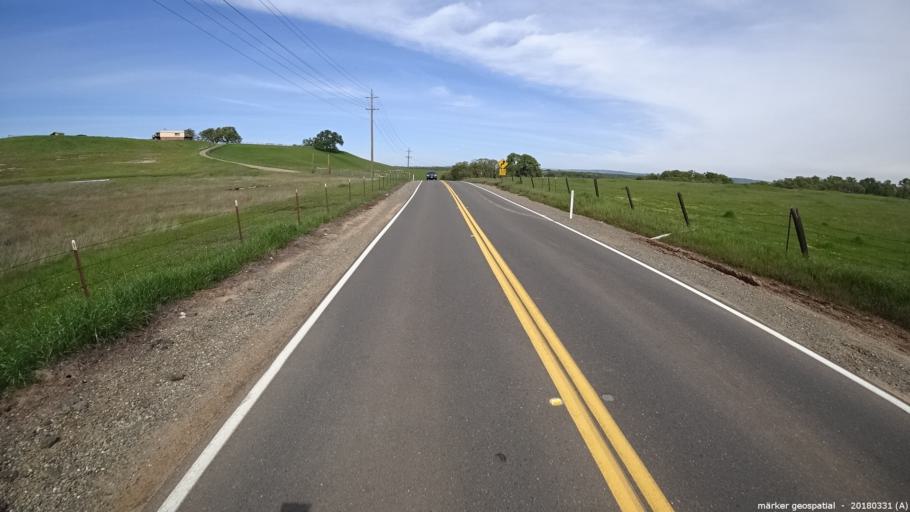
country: US
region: California
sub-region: Sacramento County
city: Rancho Murieta
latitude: 38.5151
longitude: -121.1020
